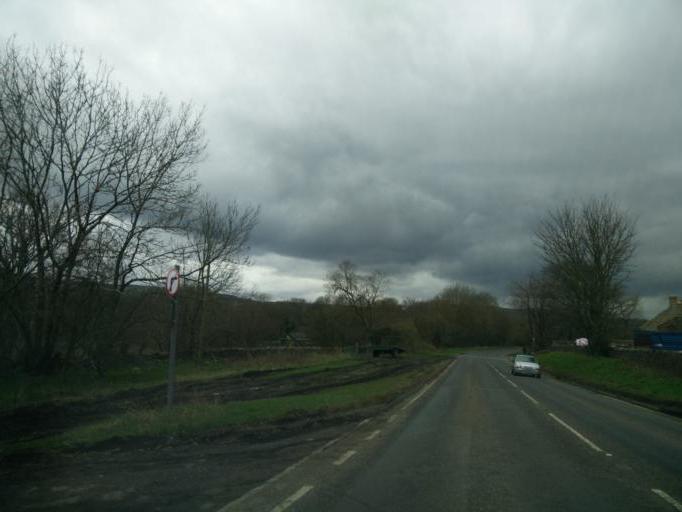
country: GB
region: England
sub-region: County Durham
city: Wolsingham
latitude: 54.7277
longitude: -1.9381
